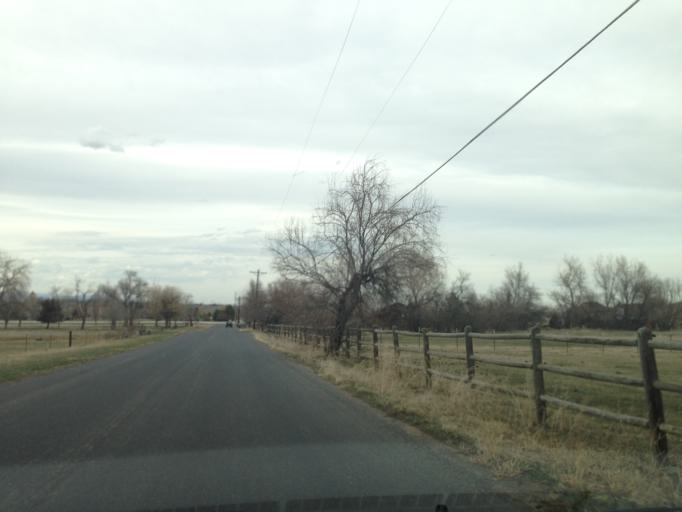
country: US
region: Colorado
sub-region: Boulder County
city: Superior
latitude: 39.9840
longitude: -105.1939
